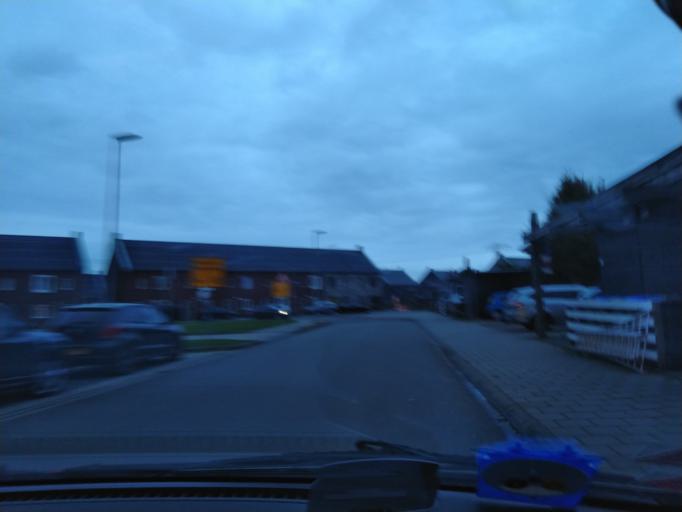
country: NL
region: Groningen
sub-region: Gemeente Groningen
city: Korrewegwijk
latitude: 53.2371
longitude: 6.5221
